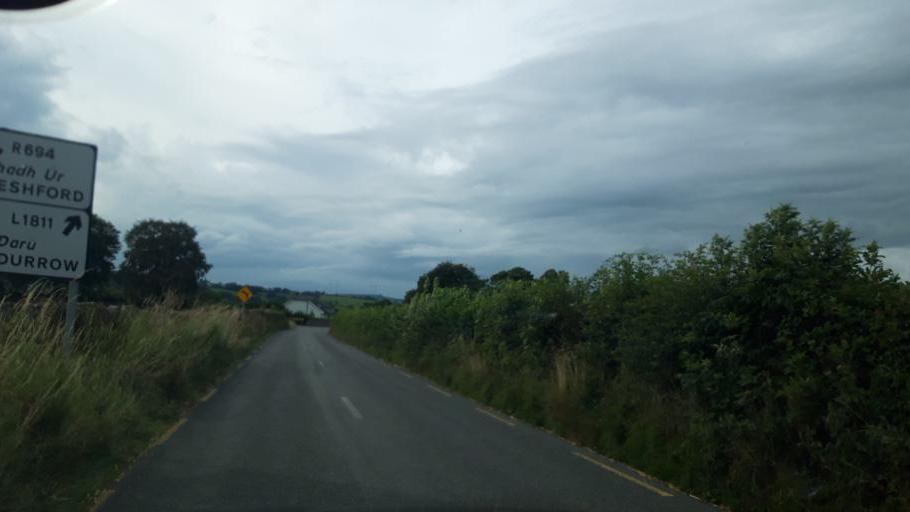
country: IE
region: Leinster
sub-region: Kilkenny
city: Ballyragget
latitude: 52.7581
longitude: -7.3775
